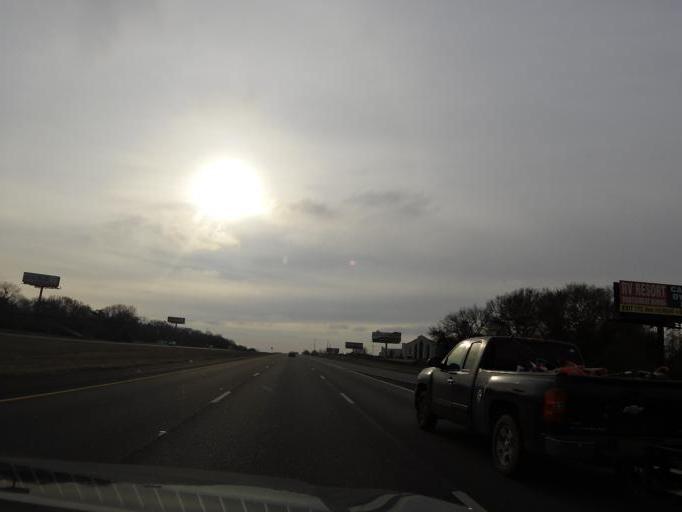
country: US
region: Alabama
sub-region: Elmore County
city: Millbrook
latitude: 32.4863
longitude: -86.4077
